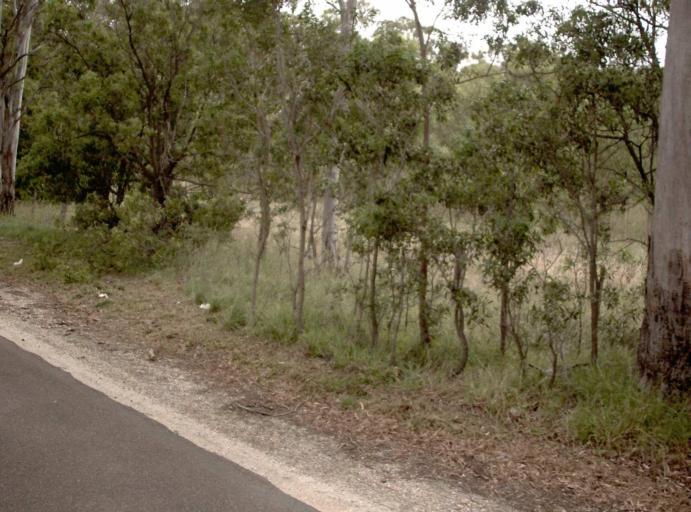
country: AU
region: Victoria
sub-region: Wellington
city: Sale
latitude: -37.8629
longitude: 147.0688
